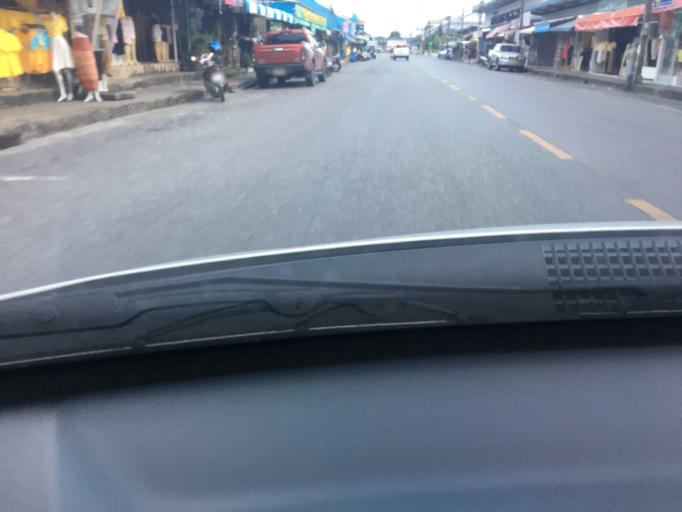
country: TH
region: Phuket
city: Ban Talat Yai
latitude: 7.8812
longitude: 98.3954
